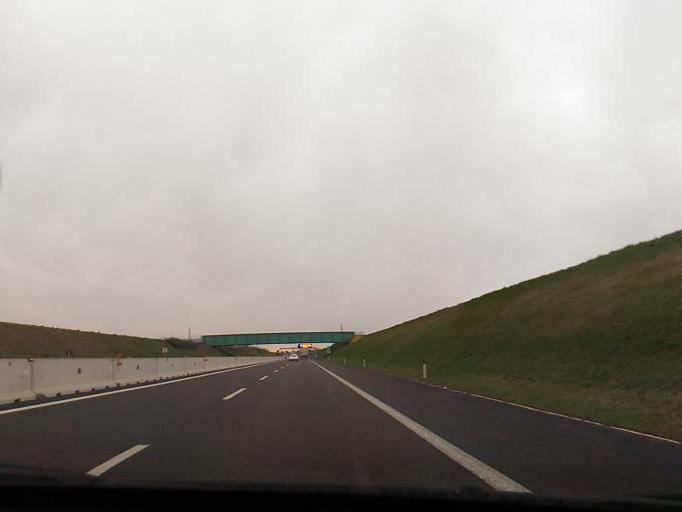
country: IT
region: Lombardy
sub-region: Provincia di Como
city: Limido Comasco
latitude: 45.6769
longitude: 8.9850
